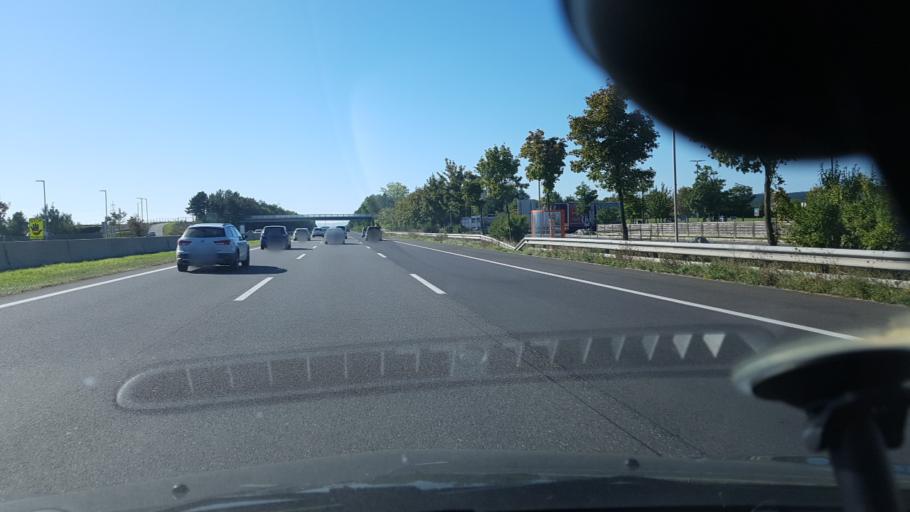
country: AT
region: Lower Austria
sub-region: Politischer Bezirk Baden
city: Leobersdorf
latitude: 47.9106
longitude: 16.2077
